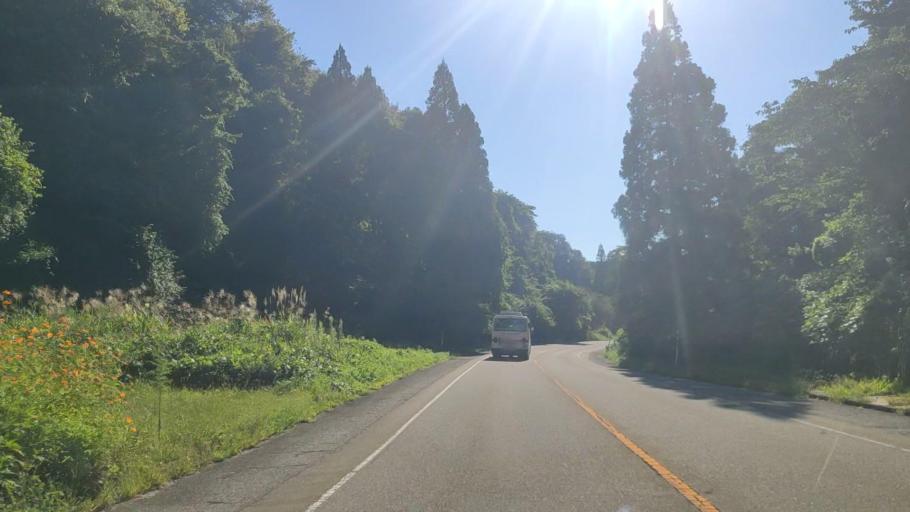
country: JP
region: Ishikawa
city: Nanao
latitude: 37.2451
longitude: 136.9910
